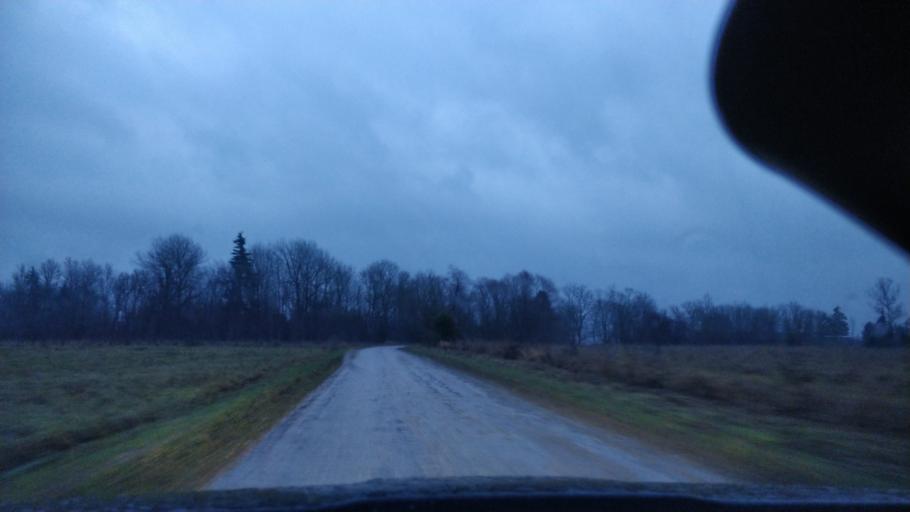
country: EE
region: Laeaene
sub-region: Lihula vald
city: Lihula
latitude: 58.8497
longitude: 23.9811
